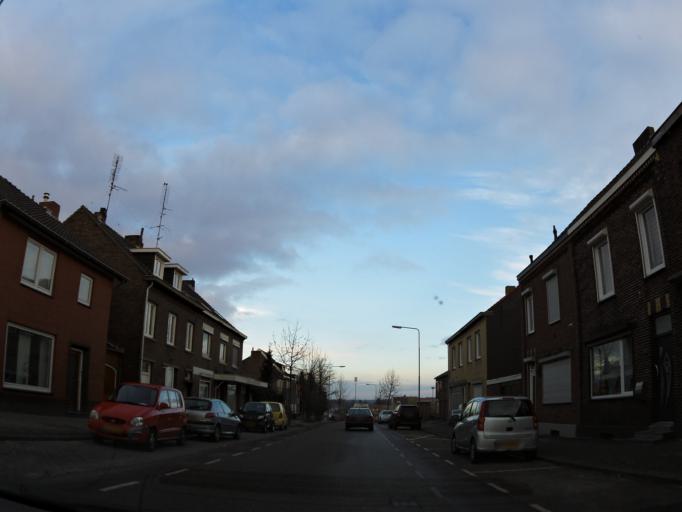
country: NL
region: Limburg
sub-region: Gemeente Onderbanken
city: Schinveld
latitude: 50.9653
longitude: 5.9826
